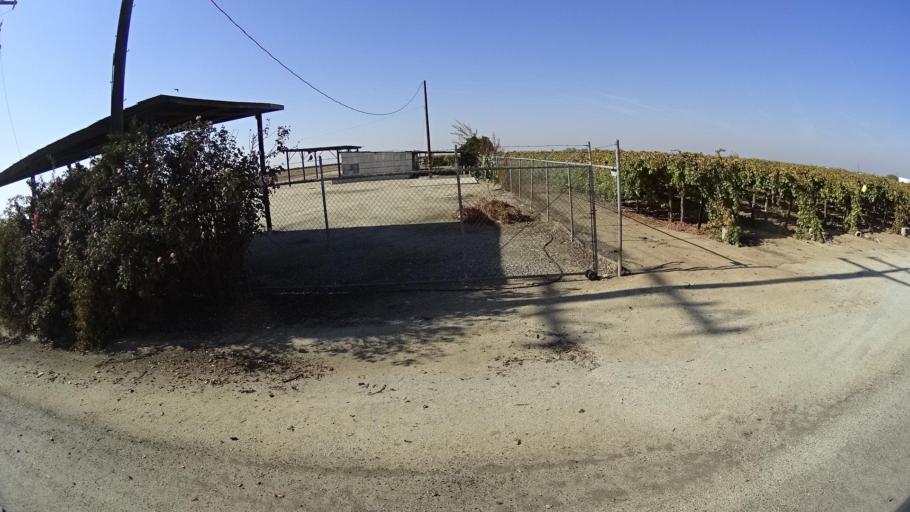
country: US
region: California
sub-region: Tulare County
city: Richgrove
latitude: 35.7365
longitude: -119.1430
